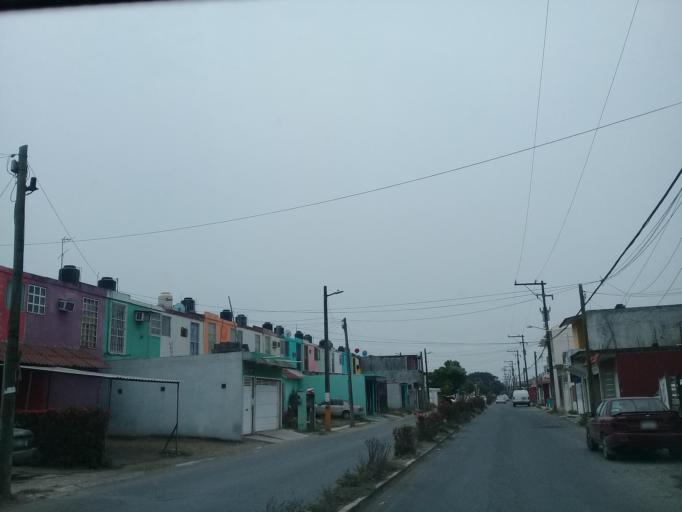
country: MX
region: Veracruz
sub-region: Veracruz
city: Las Amapolas
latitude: 19.1577
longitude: -96.2070
